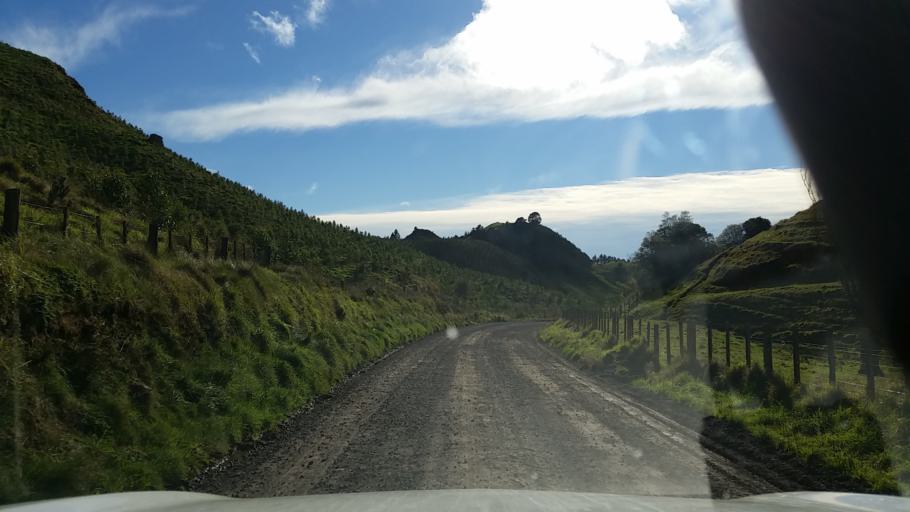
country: NZ
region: Bay of Plenty
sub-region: Rotorua District
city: Rotorua
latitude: -38.3637
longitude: 176.2080
